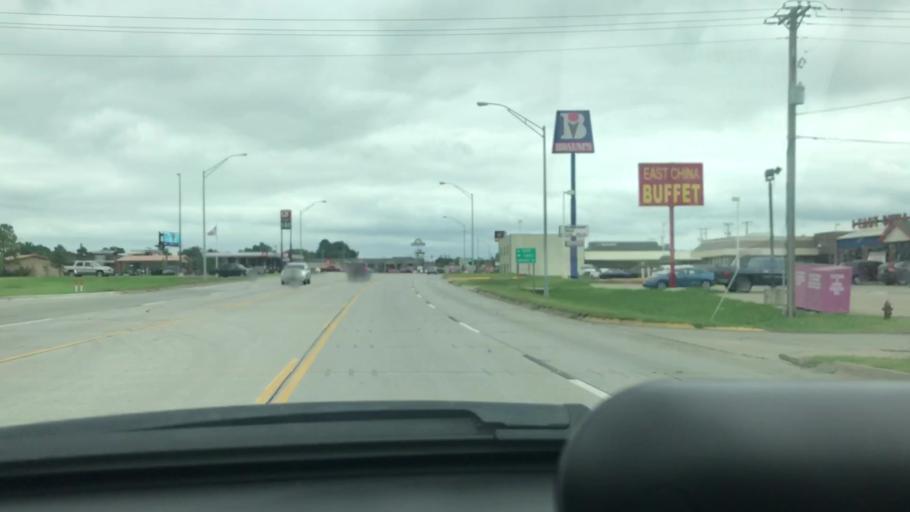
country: US
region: Oklahoma
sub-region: Wagoner County
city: Wagoner
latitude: 35.9563
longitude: -95.3952
